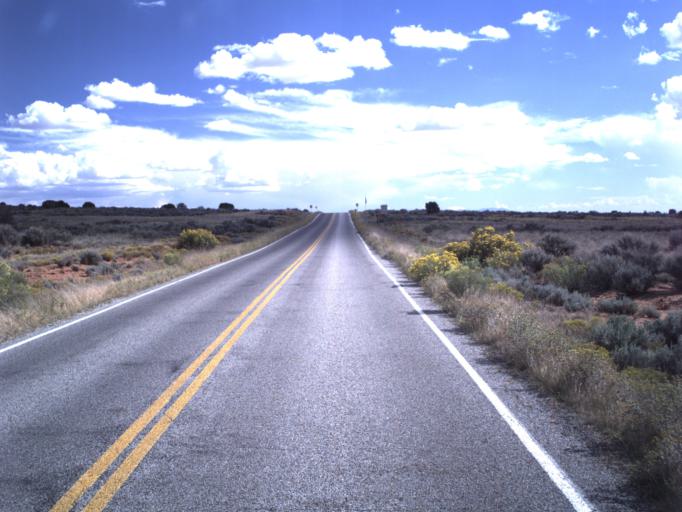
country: US
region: Utah
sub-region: Grand County
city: Moab
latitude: 38.5200
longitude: -109.7317
